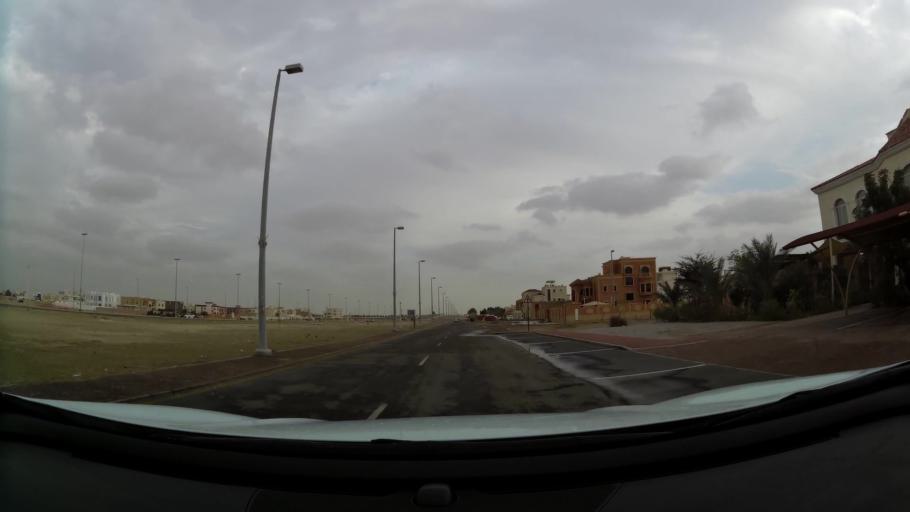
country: AE
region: Abu Dhabi
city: Abu Dhabi
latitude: 24.3466
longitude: 54.6264
